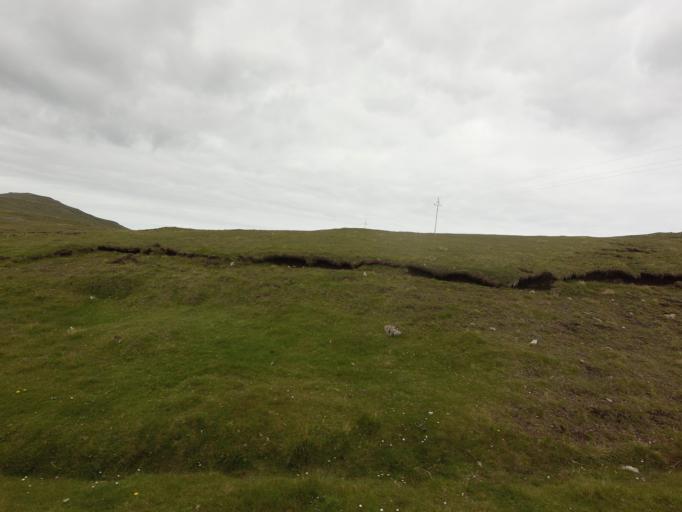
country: FO
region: Suduroy
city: Vagur
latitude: 61.4306
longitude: -6.7588
